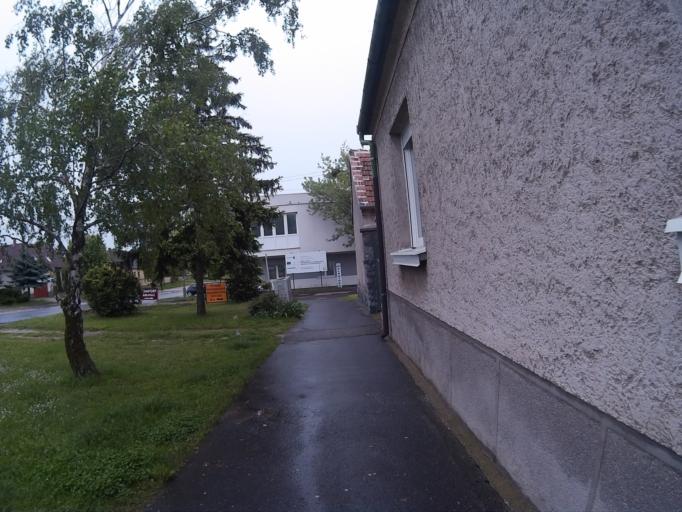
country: HU
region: Veszprem
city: Sumeg
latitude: 46.9759
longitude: 17.2829
